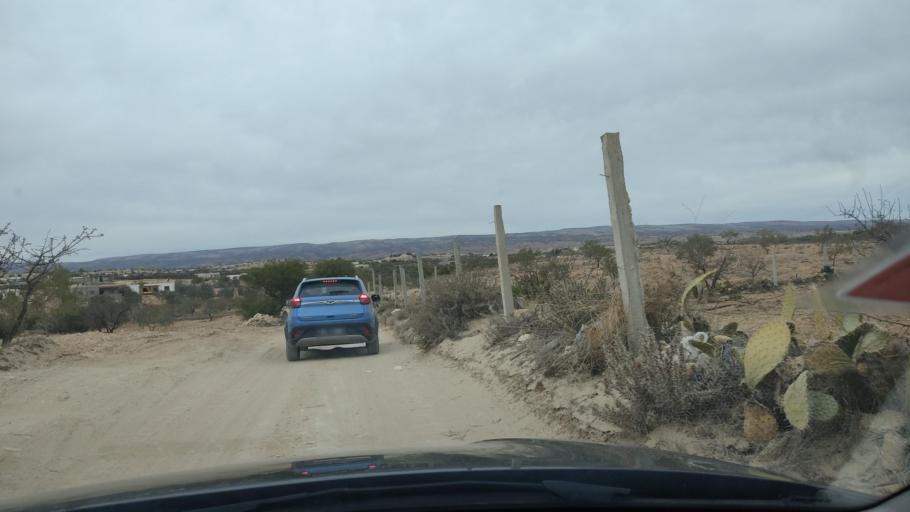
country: TN
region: Al Qasrayn
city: Kasserine
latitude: 35.2294
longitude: 8.9123
